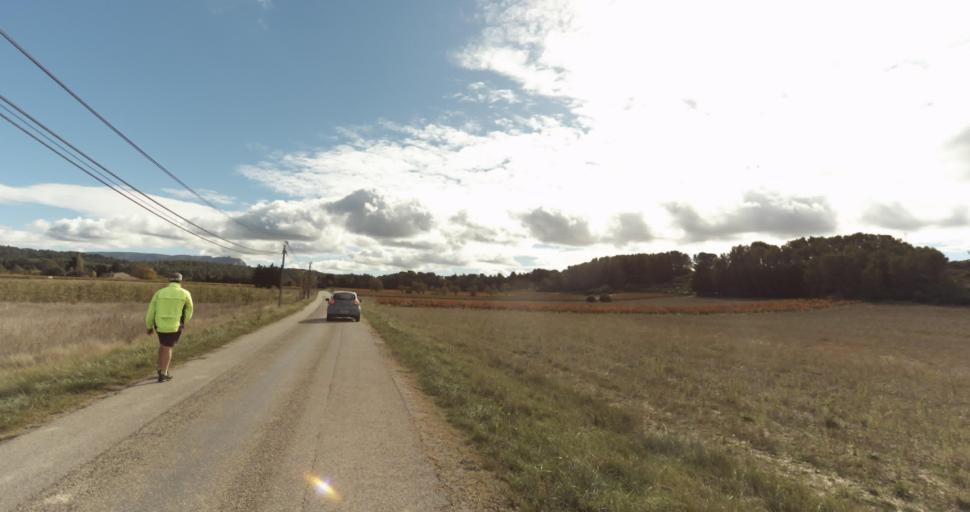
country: FR
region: Provence-Alpes-Cote d'Azur
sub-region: Departement des Bouches-du-Rhone
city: Venelles
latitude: 43.5821
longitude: 5.4941
